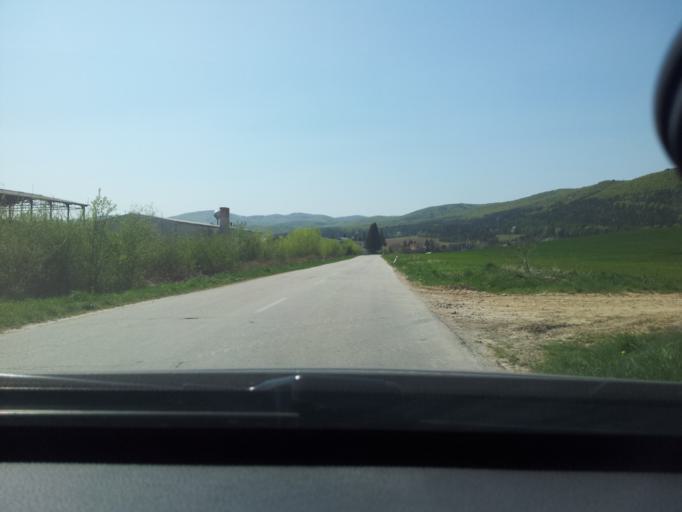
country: SK
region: Nitriansky
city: Partizanske
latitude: 48.5695
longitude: 18.3186
